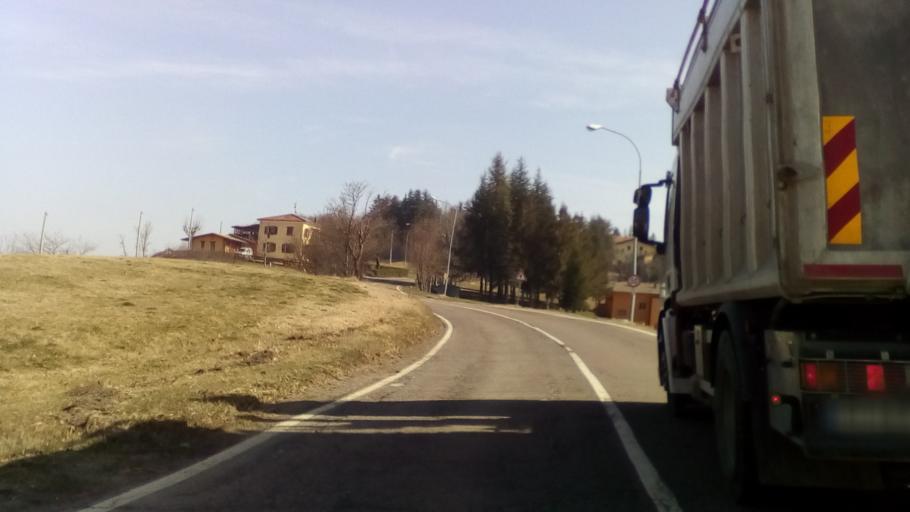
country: IT
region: Emilia-Romagna
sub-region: Provincia di Modena
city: Lama
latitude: 44.3113
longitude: 10.7737
